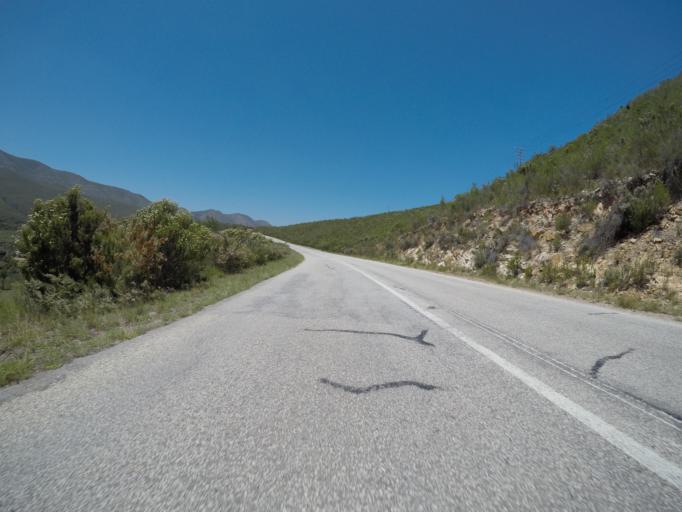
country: ZA
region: Eastern Cape
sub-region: Cacadu District Municipality
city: Kareedouw
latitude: -33.8851
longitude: 24.0717
